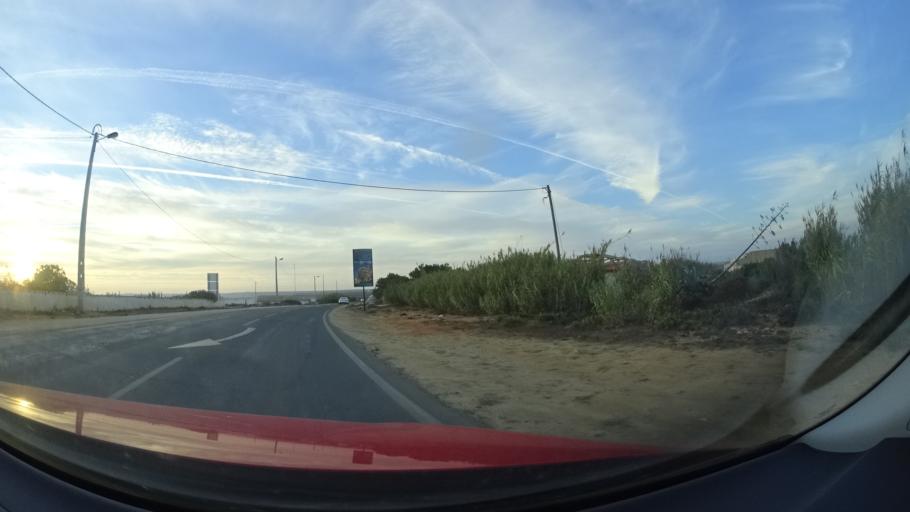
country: PT
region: Faro
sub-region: Vila do Bispo
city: Sagres
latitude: 37.0091
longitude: -8.9482
